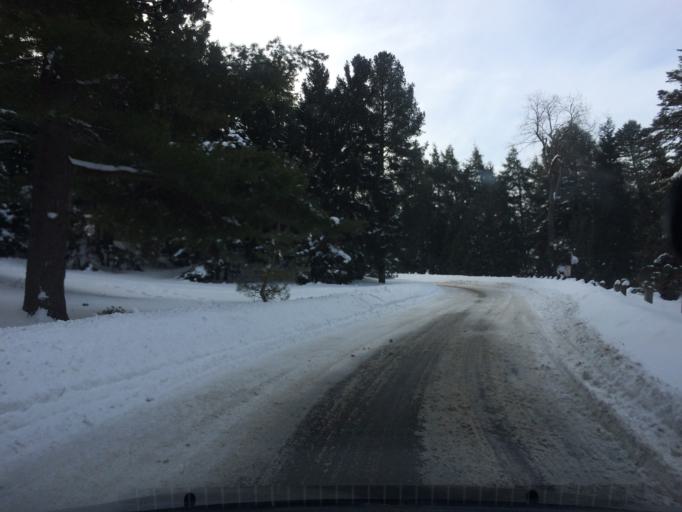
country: US
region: New York
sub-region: Monroe County
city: Rochester
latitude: 43.1336
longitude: -77.6050
